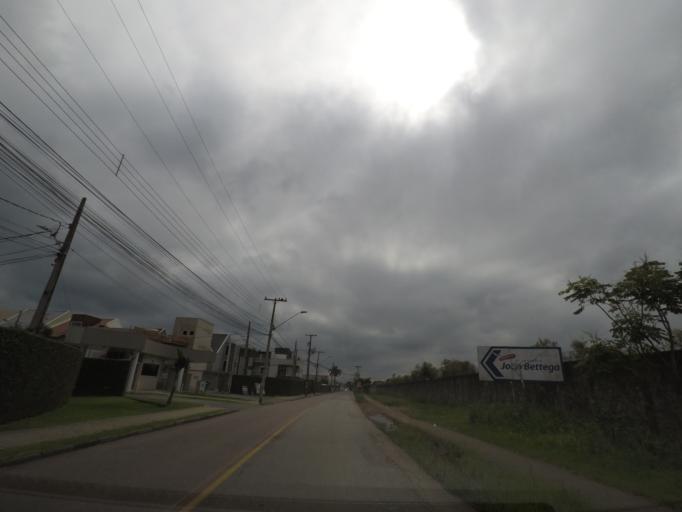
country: BR
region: Parana
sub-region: Curitiba
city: Curitiba
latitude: -25.5088
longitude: -49.3344
